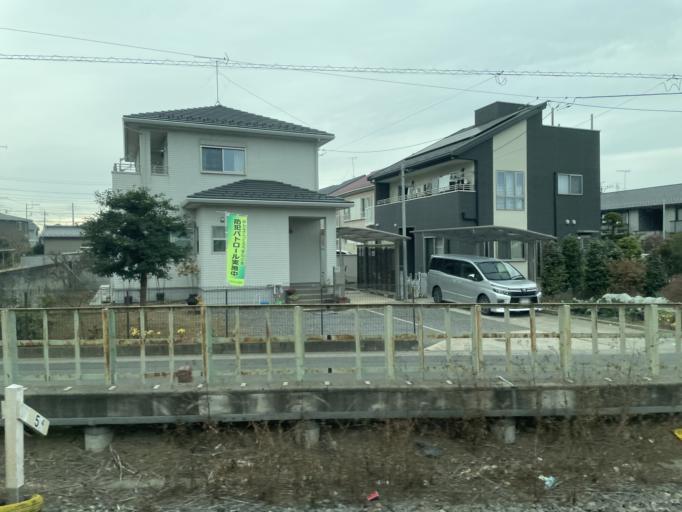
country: JP
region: Saitama
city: Shiraoka
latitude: 36.0109
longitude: 139.6657
